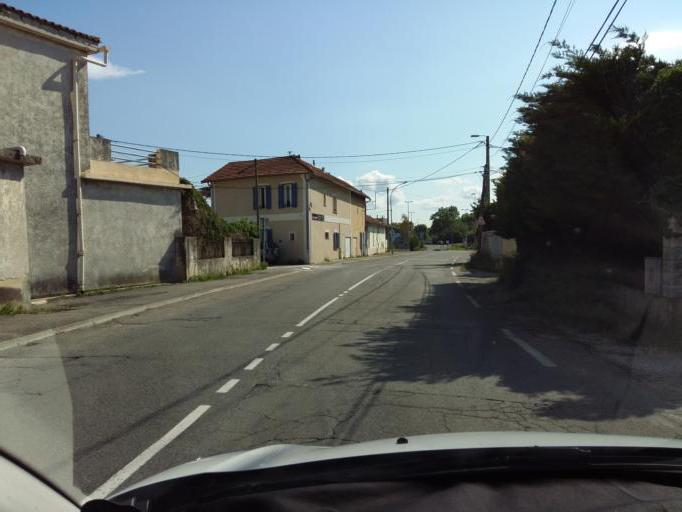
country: FR
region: Provence-Alpes-Cote d'Azur
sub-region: Departement du Vaucluse
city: Cavaillon
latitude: 43.8450
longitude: 5.0458
